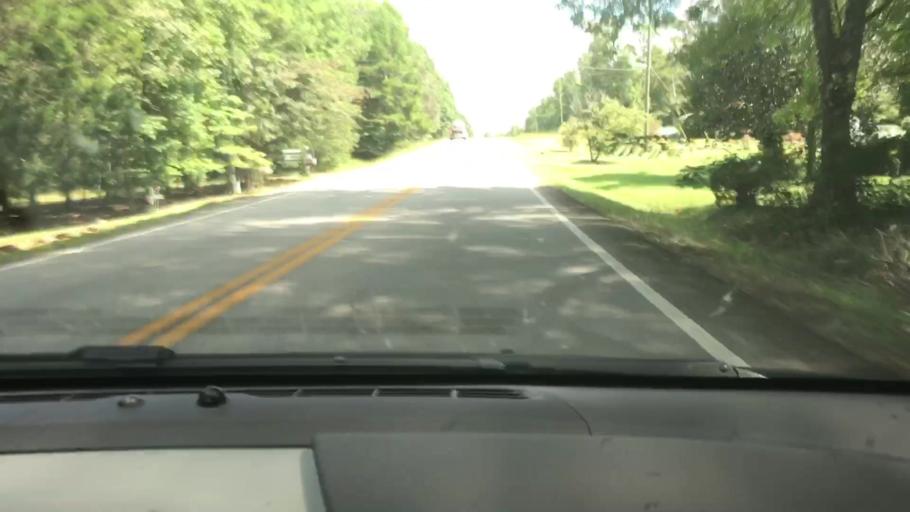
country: US
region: Georgia
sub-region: Troup County
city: La Grange
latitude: 32.9093
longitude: -85.0229
